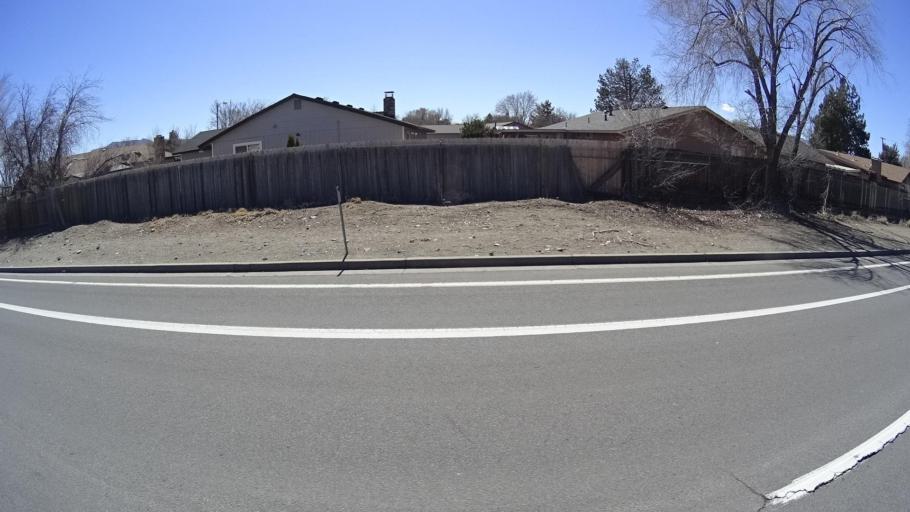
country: US
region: Nevada
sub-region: Washoe County
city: Sparks
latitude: 39.5563
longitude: -119.7377
